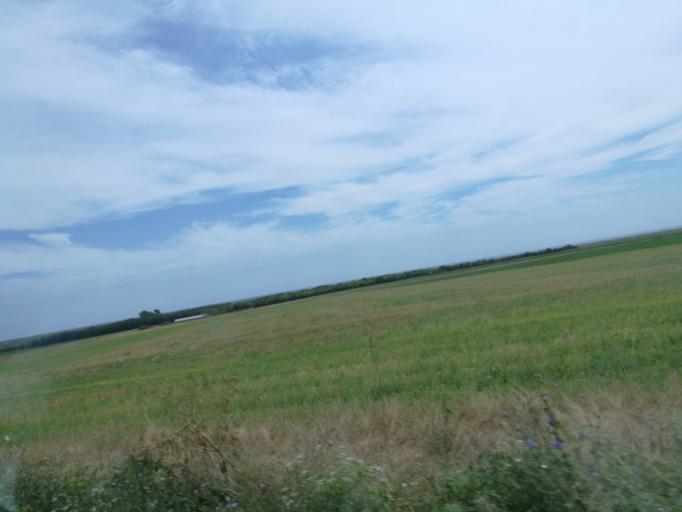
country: RO
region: Constanta
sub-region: Comuna Corbu
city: Corbu
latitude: 44.4325
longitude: 28.7187
